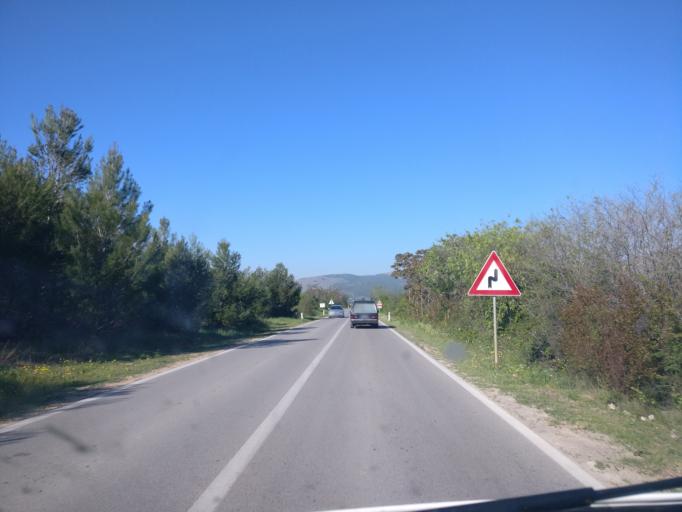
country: BA
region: Federation of Bosnia and Herzegovina
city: Tasovcici
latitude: 43.1191
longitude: 17.7291
